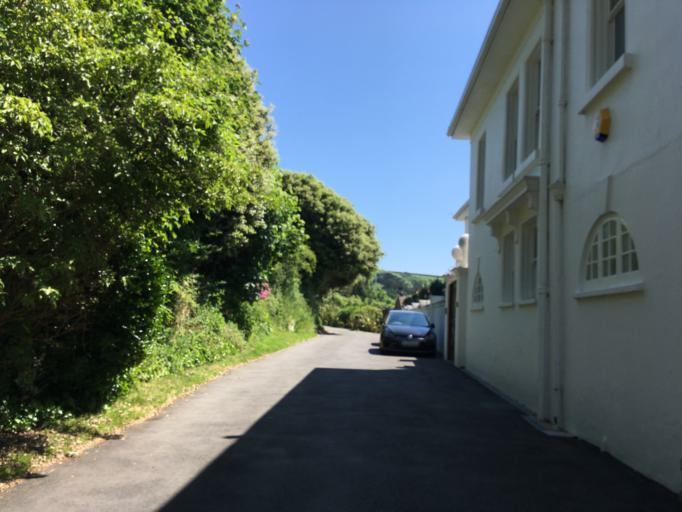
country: GB
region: England
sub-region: Devon
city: Dartmouth
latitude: 50.3431
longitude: -3.5594
